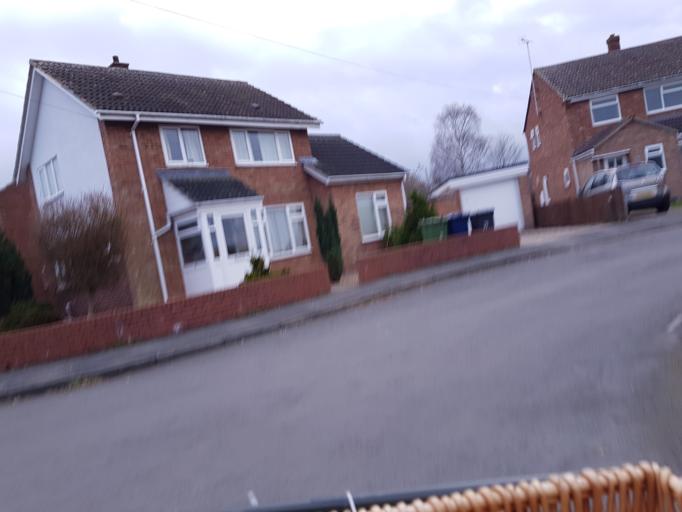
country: GB
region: England
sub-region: Cambridgeshire
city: Fulbourn
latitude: 52.1962
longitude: 0.1782
